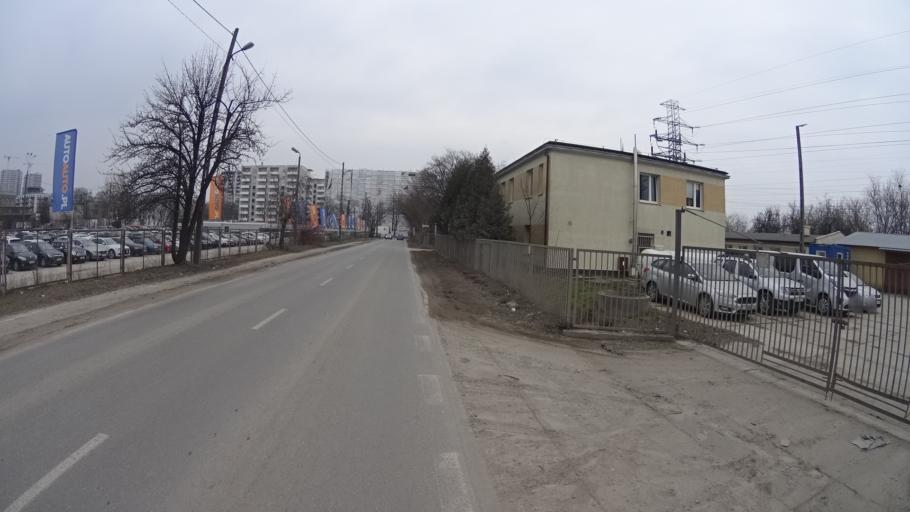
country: PL
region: Masovian Voivodeship
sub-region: Warszawa
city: Ochota
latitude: 52.2204
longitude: 20.9528
